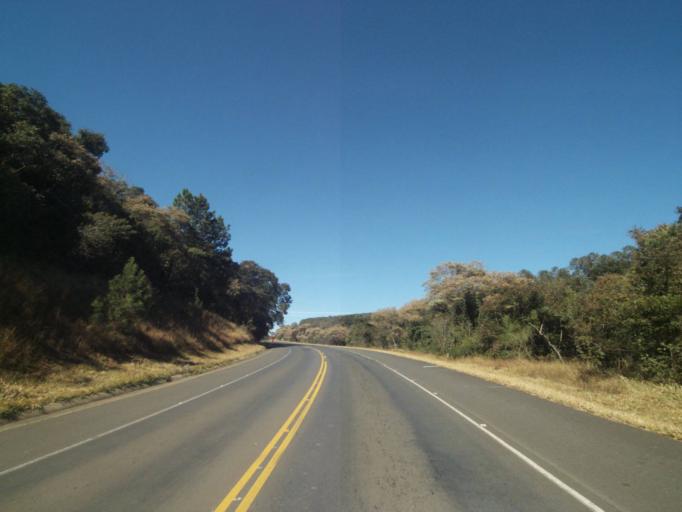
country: BR
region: Parana
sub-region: Tibagi
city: Tibagi
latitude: -24.5539
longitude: -50.4566
